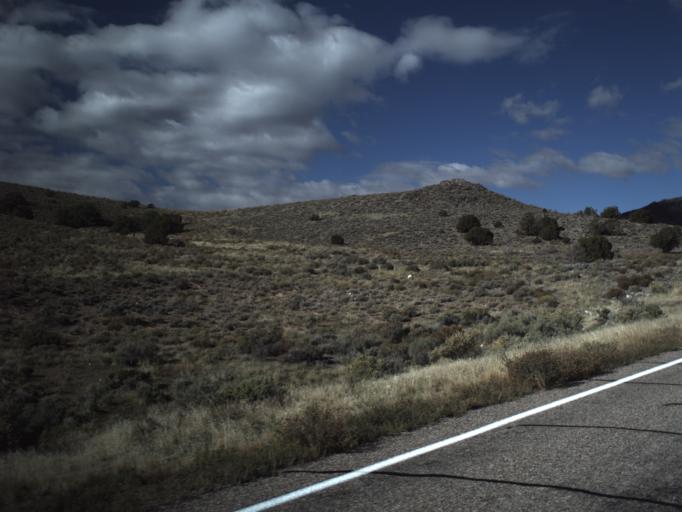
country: US
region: Utah
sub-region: Beaver County
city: Milford
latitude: 38.4578
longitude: -113.2276
